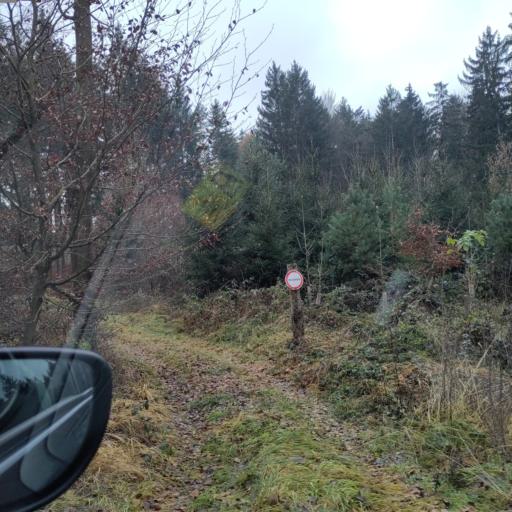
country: AT
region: Lower Austria
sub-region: Politischer Bezirk Sankt Polten
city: Neidling
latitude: 48.2695
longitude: 15.5198
